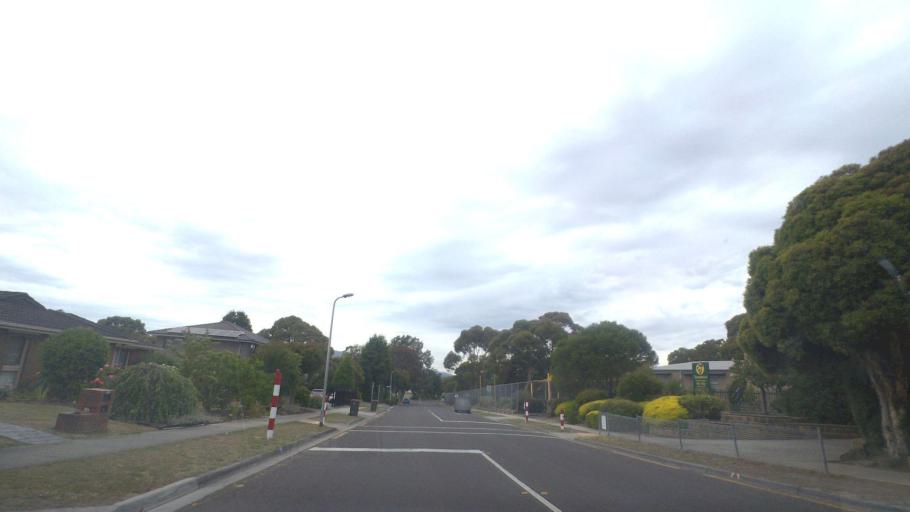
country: AU
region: Victoria
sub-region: Knox
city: Wantirna
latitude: -37.8607
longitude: 145.2322
